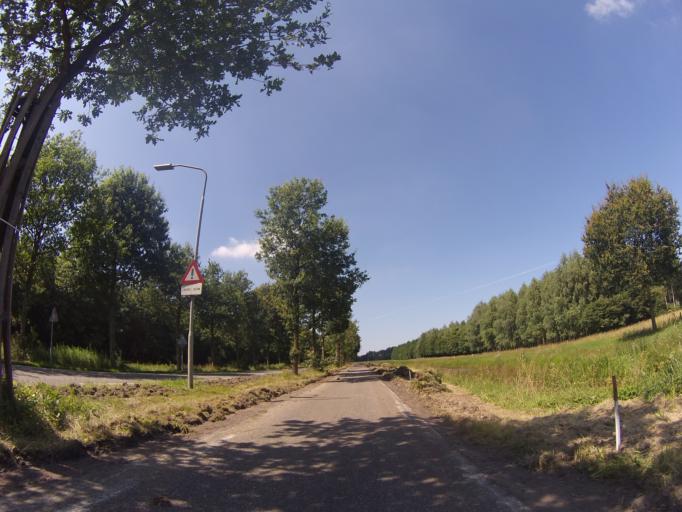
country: NL
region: Drenthe
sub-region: Gemeente Emmen
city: Klazienaveen
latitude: 52.7570
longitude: 6.9989
